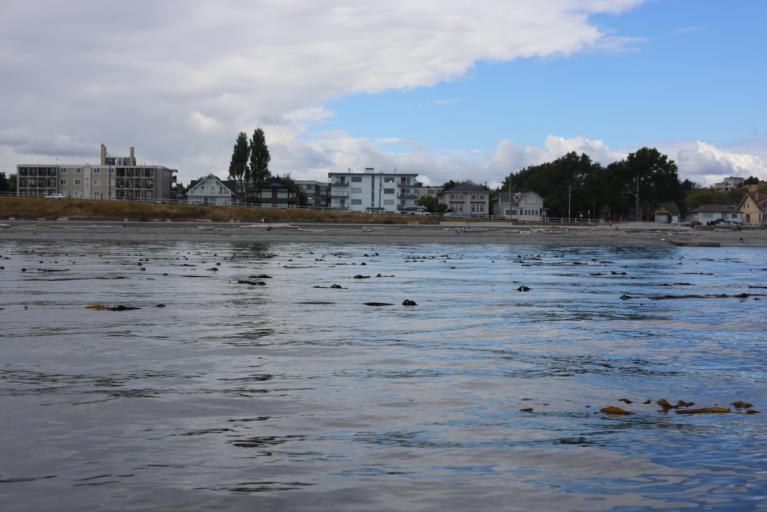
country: CA
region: British Columbia
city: Victoria
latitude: 48.4063
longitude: -123.3442
